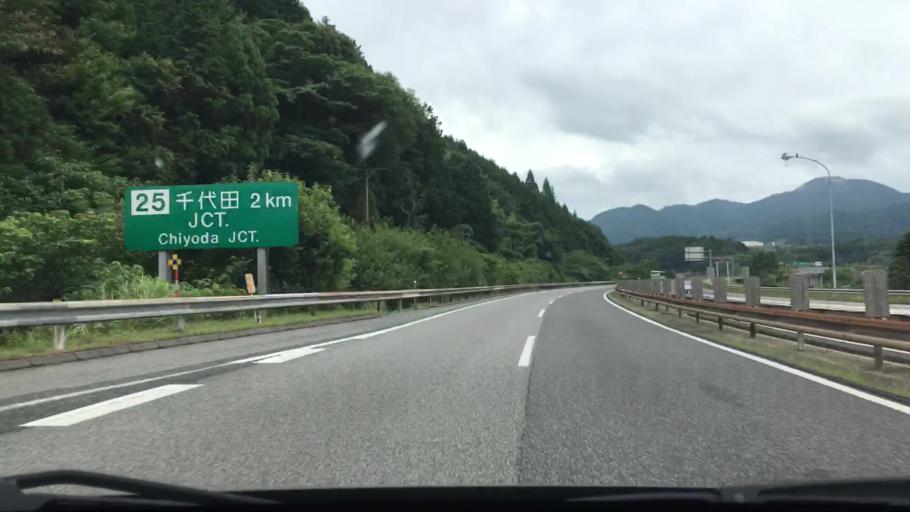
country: JP
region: Hiroshima
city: Hiroshima-shi
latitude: 34.6708
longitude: 132.5412
